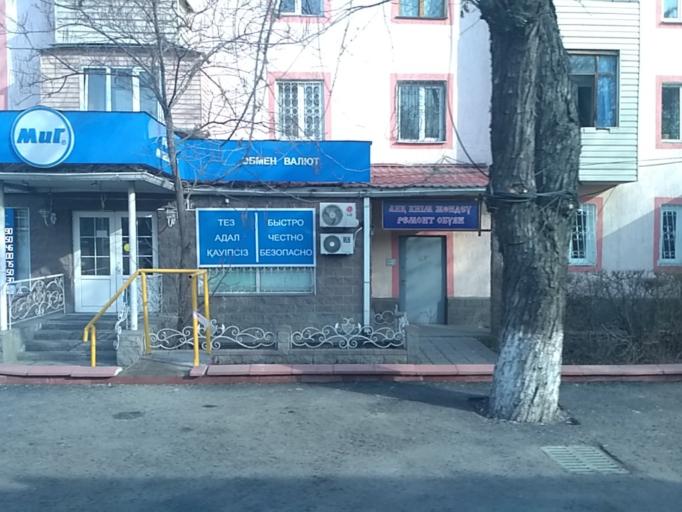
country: KZ
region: Almaty Qalasy
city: Almaty
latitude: 43.2261
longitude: 76.9073
